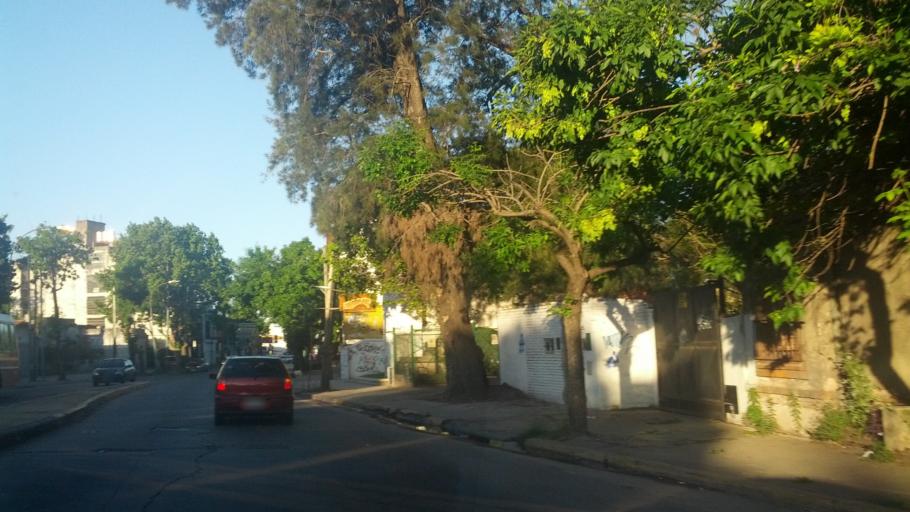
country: AR
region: Buenos Aires
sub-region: Partido de Lomas de Zamora
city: Lomas de Zamora
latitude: -34.7785
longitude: -58.3937
